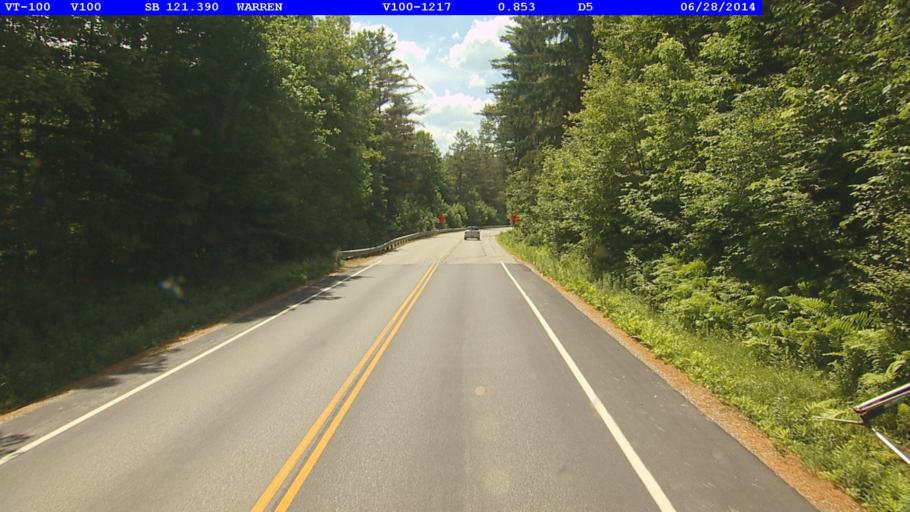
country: US
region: Vermont
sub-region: Washington County
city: Northfield
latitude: 44.0718
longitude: -72.8600
